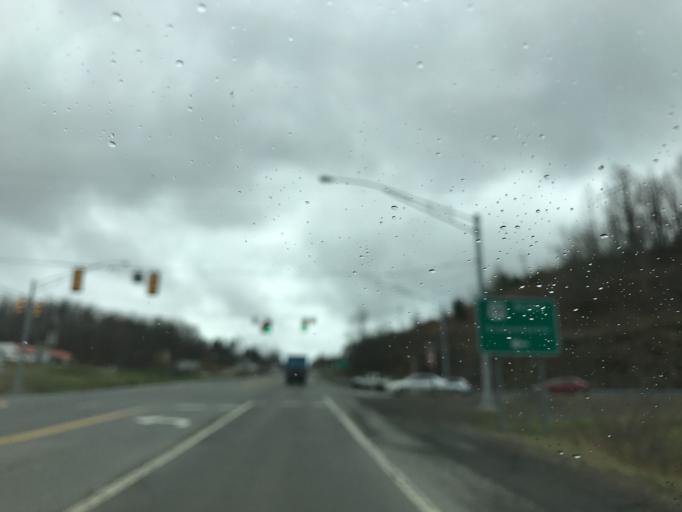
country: US
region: West Virginia
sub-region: Raleigh County
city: Bradley
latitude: 37.8509
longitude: -81.1968
